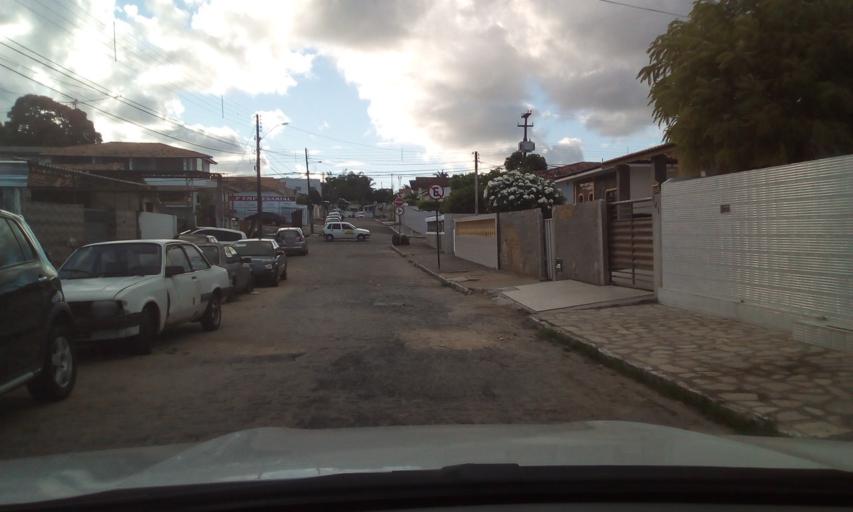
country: BR
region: Paraiba
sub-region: Joao Pessoa
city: Joao Pessoa
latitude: -7.1302
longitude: -34.8644
